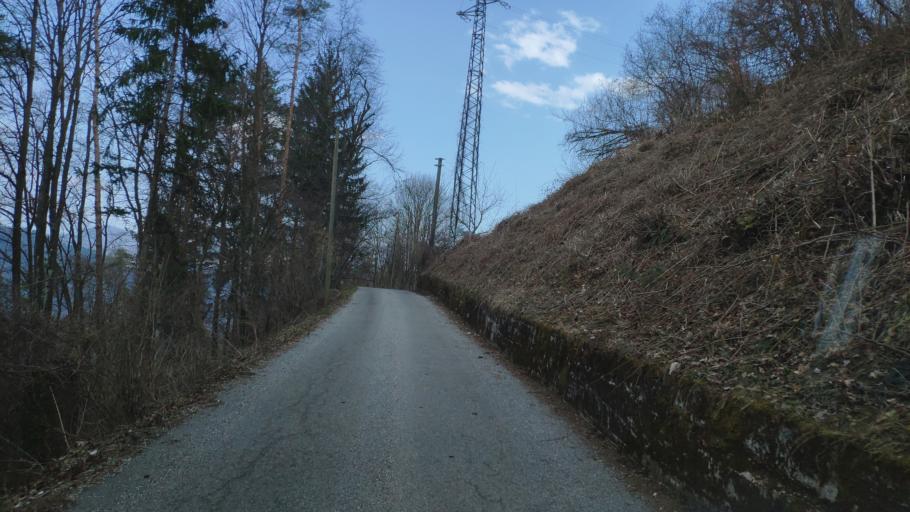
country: IT
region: Veneto
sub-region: Provincia di Vicenza
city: Enego
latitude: 45.9501
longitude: 11.7053
